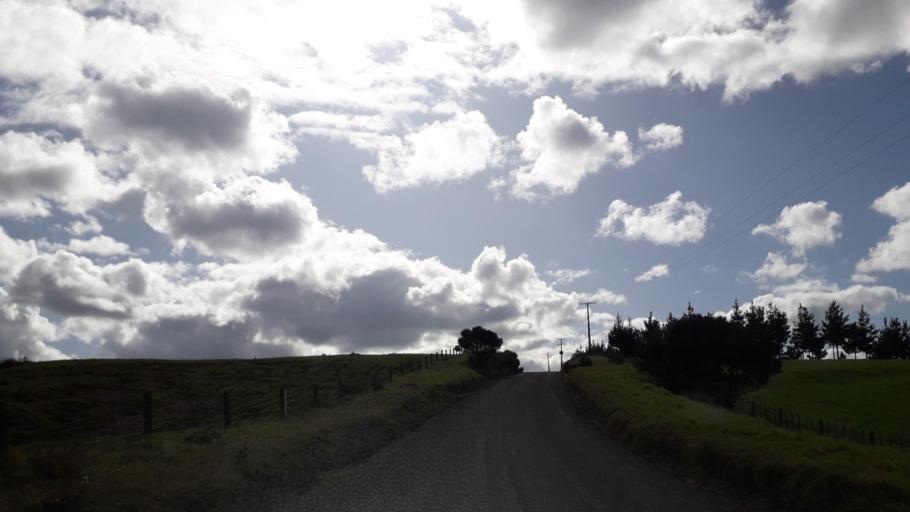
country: NZ
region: Northland
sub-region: Far North District
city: Kerikeri
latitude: -35.1349
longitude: 174.0175
